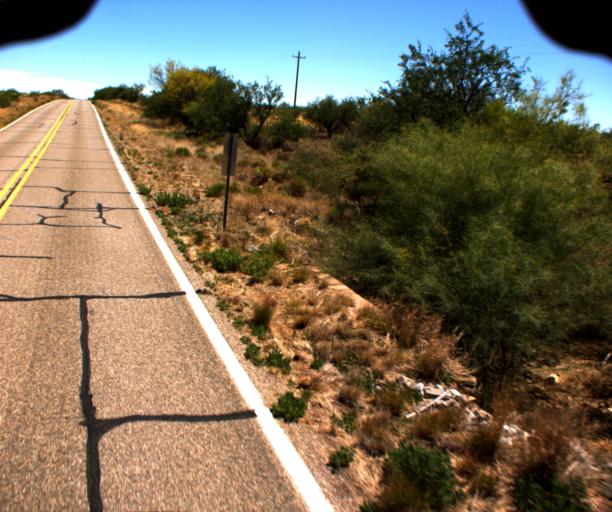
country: US
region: Arizona
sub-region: Pima County
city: Three Points
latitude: 31.7285
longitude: -111.4880
